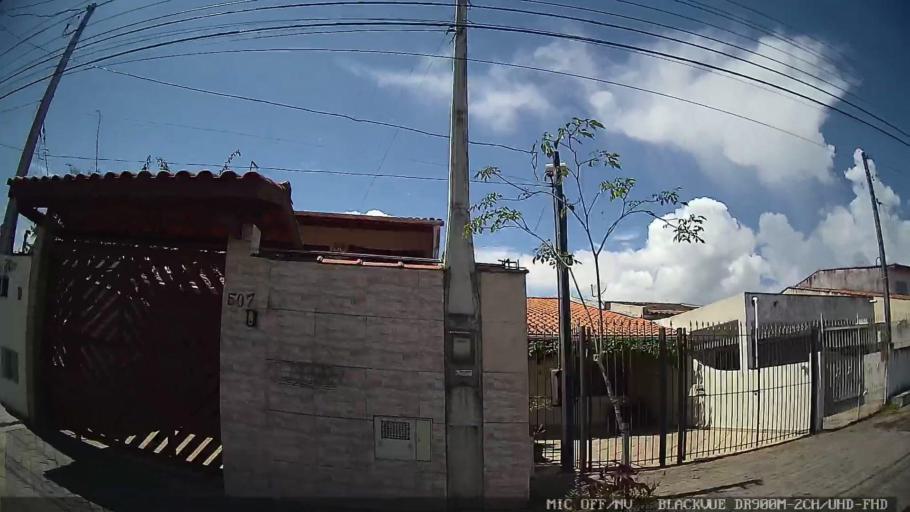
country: BR
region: Sao Paulo
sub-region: Caraguatatuba
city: Caraguatatuba
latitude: -23.6728
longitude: -45.4357
